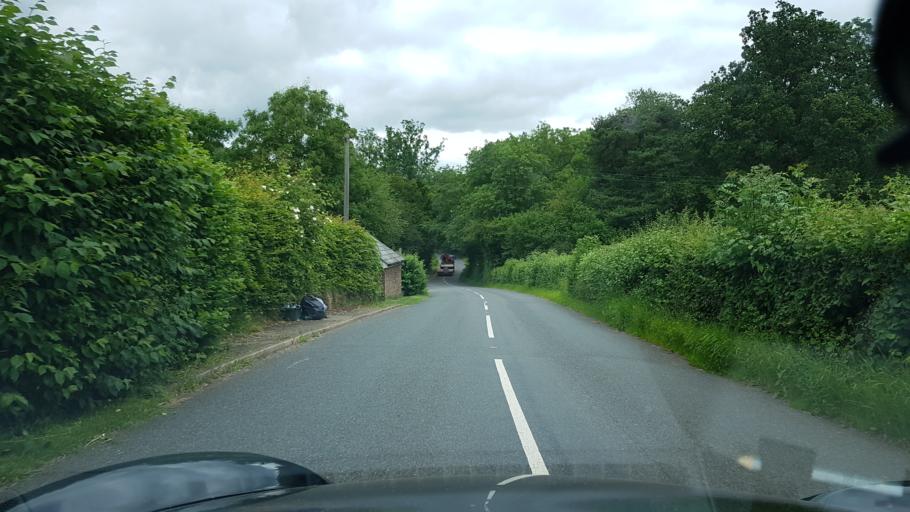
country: GB
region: England
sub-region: Herefordshire
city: Llanrothal
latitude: 51.8750
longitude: -2.8188
